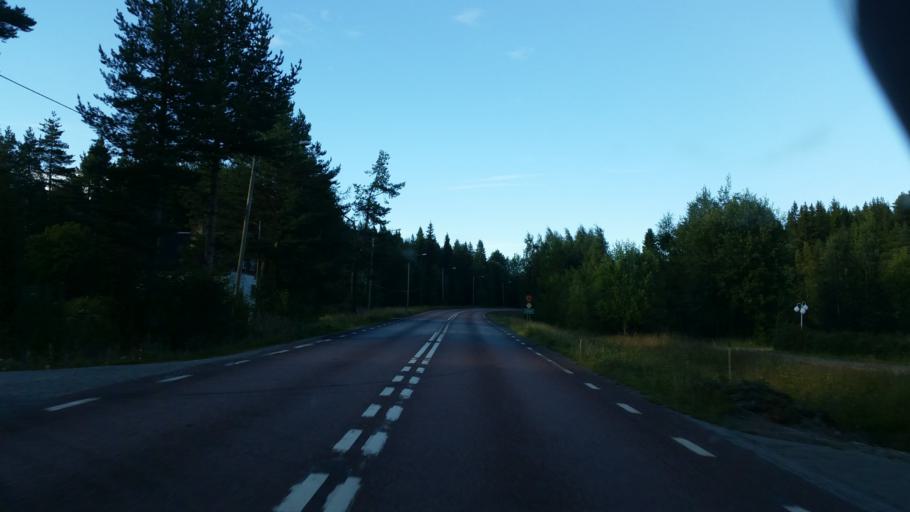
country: SE
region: Vaesterbotten
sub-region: Dorotea Kommun
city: Dorotea
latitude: 64.1613
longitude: 16.2646
